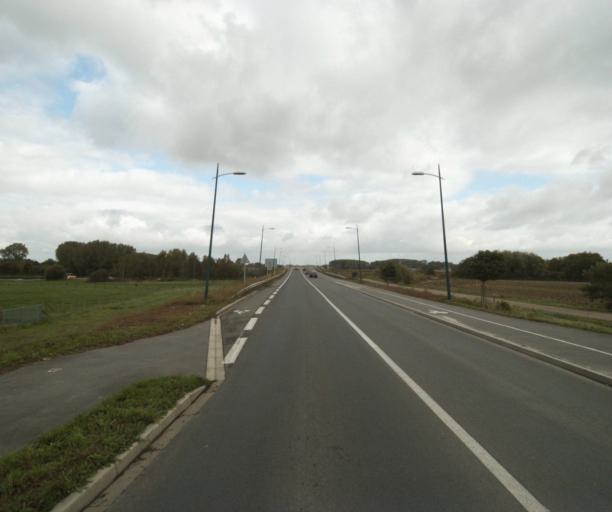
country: FR
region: Nord-Pas-de-Calais
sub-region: Departement du Nord
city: Verlinghem
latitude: 50.6954
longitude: 3.0219
